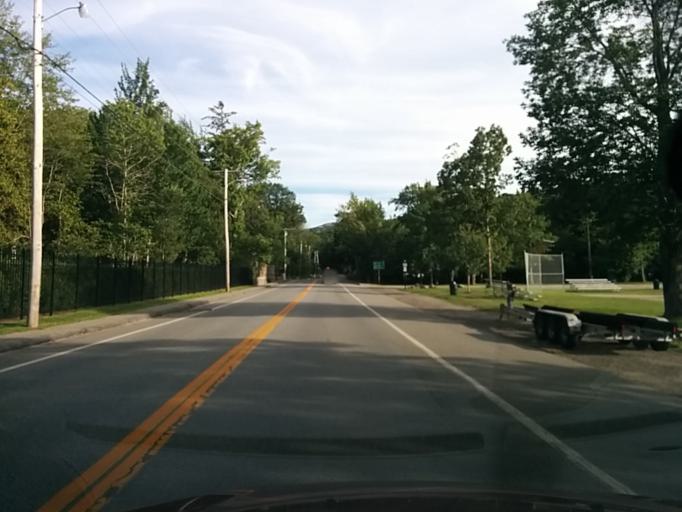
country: US
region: Maine
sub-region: Hancock County
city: Bar Harbor
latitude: 44.3823
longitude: -68.2028
